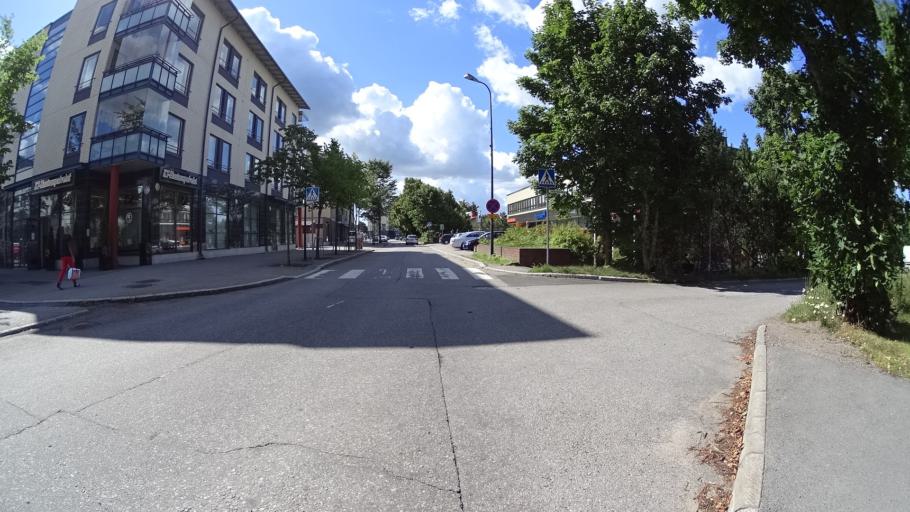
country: FI
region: Uusimaa
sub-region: Helsinki
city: Tuusula
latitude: 60.4004
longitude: 25.0223
